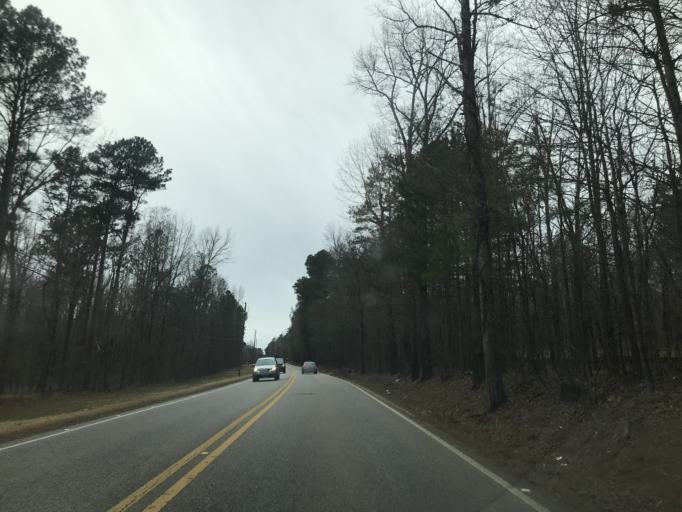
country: US
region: Alabama
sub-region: Shelby County
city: Brook Highland
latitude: 33.4573
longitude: -86.6473
